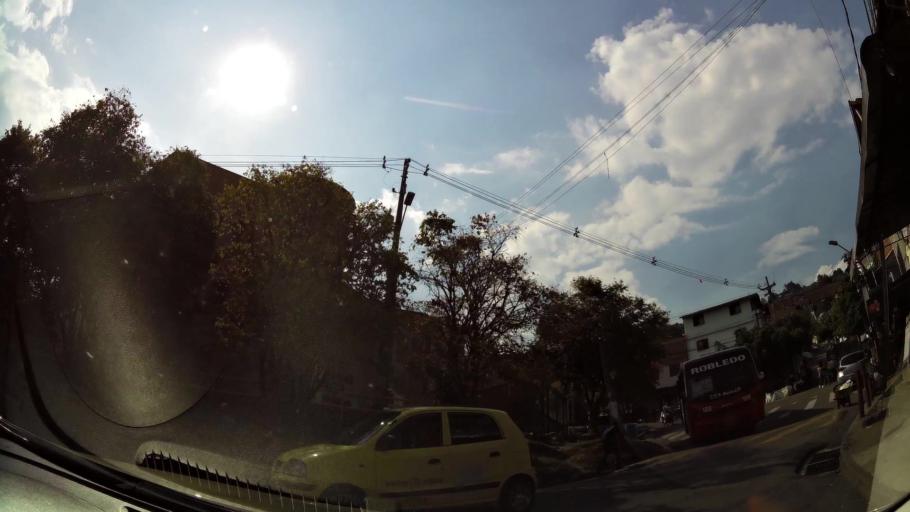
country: CO
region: Antioquia
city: Medellin
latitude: 6.2928
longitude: -75.5935
